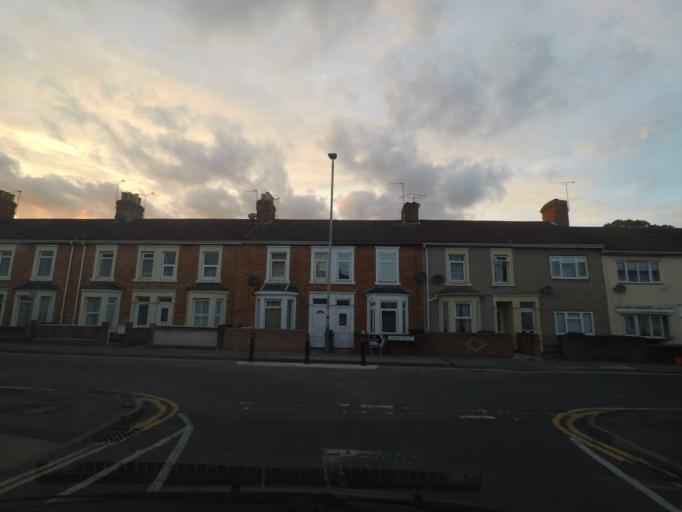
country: GB
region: England
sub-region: Borough of Swindon
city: Swindon
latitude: 51.5587
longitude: -1.7892
